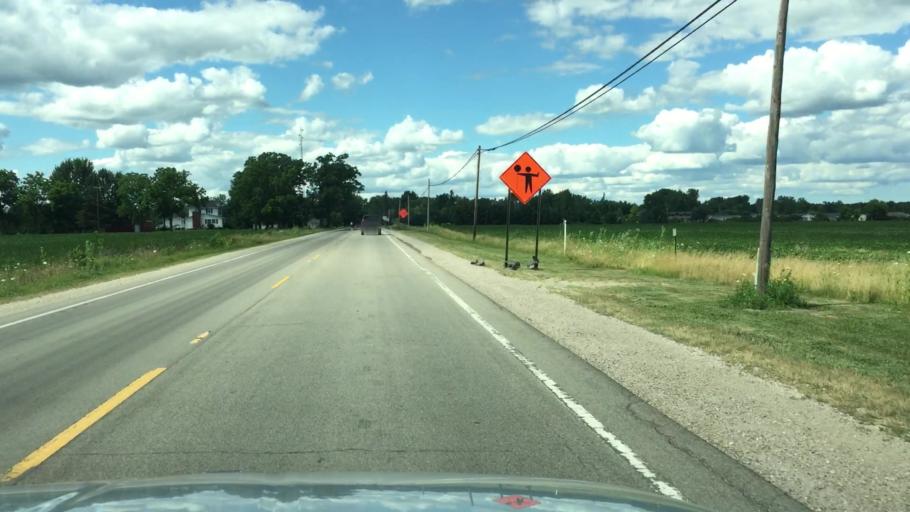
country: US
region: Michigan
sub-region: Saint Clair County
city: Capac
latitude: 43.0009
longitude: -82.9282
